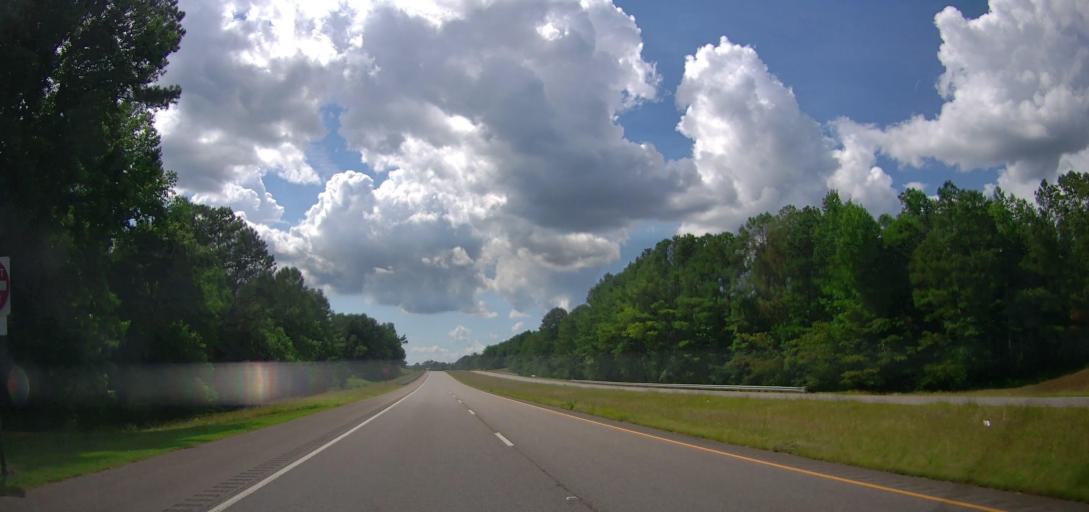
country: US
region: Alabama
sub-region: Pickens County
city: Reform
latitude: 33.4008
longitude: -88.0678
